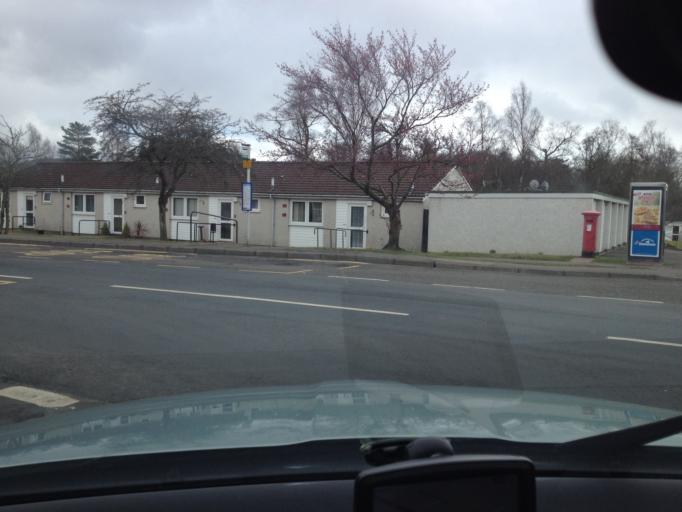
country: GB
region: Scotland
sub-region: Perth and Kinross
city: Scone
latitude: 56.4234
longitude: -3.4107
